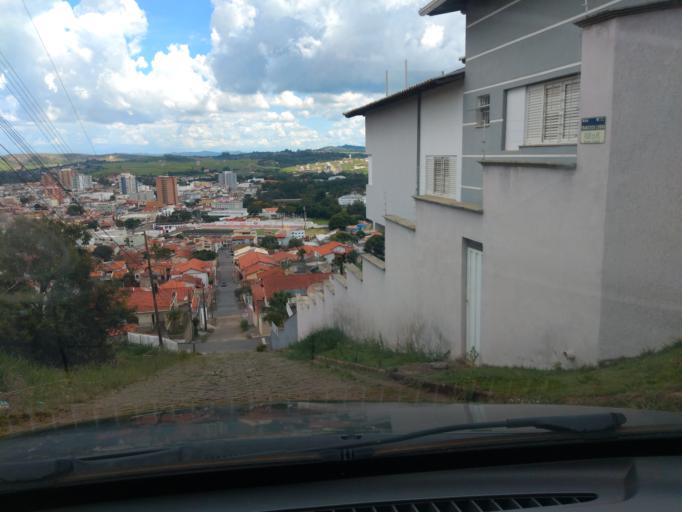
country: BR
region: Minas Gerais
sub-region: Tres Coracoes
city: Tres Coracoes
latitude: -21.6913
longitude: -45.2631
